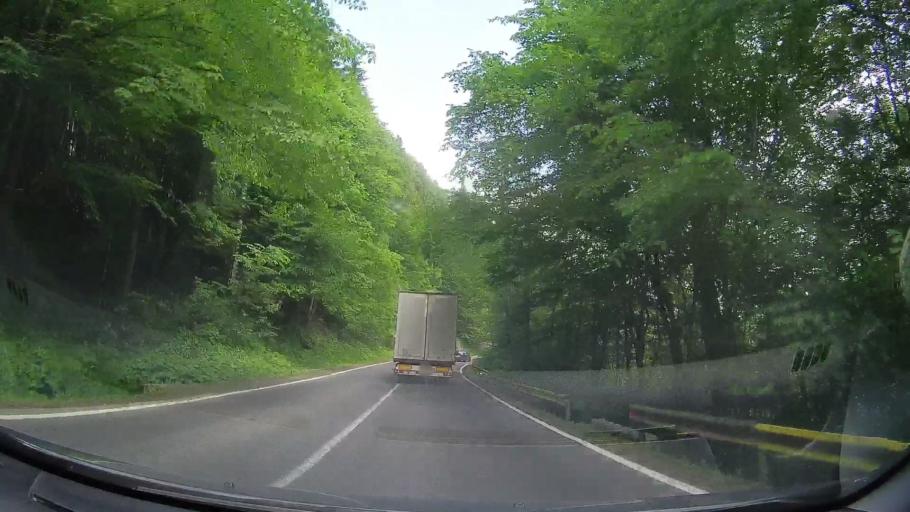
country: RO
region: Prahova
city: Maneciu
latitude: 45.3748
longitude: 25.9294
